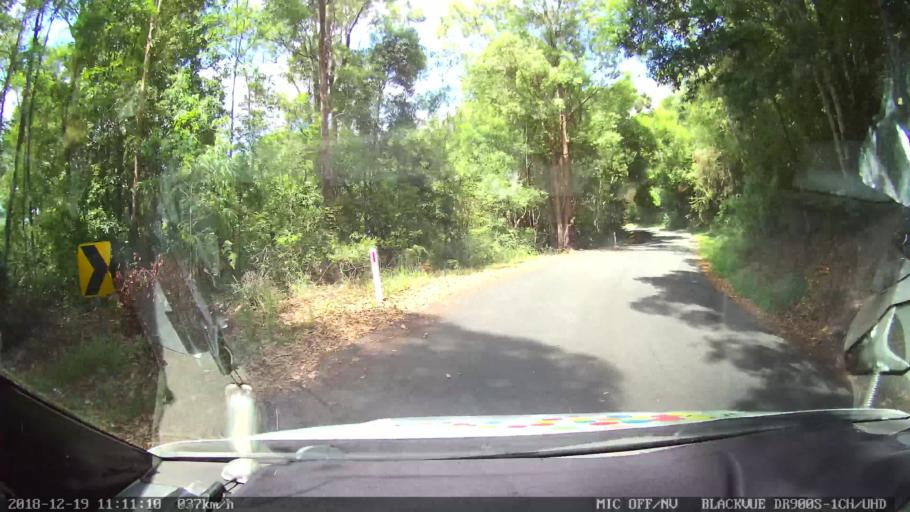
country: AU
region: New South Wales
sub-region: Lismore Municipality
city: Nimbin
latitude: -28.6421
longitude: 153.2584
